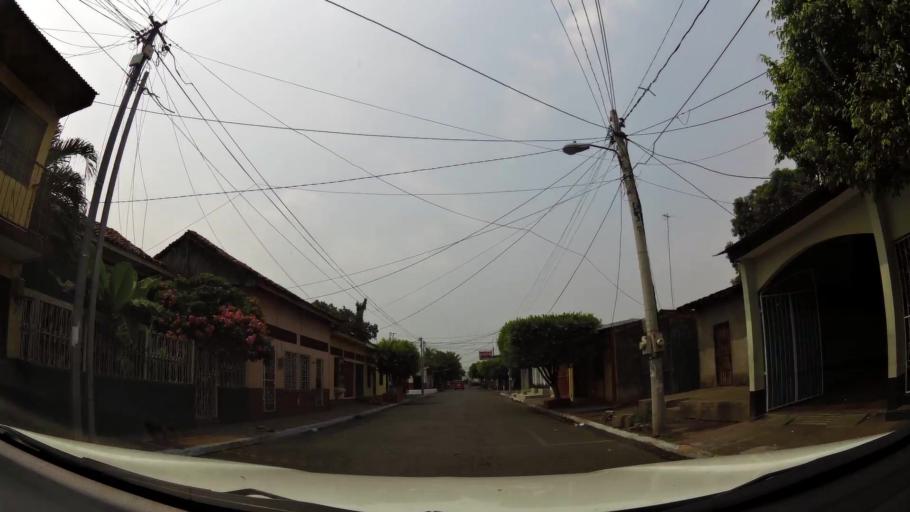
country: NI
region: Chinandega
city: Chinandega
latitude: 12.6264
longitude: -87.1344
